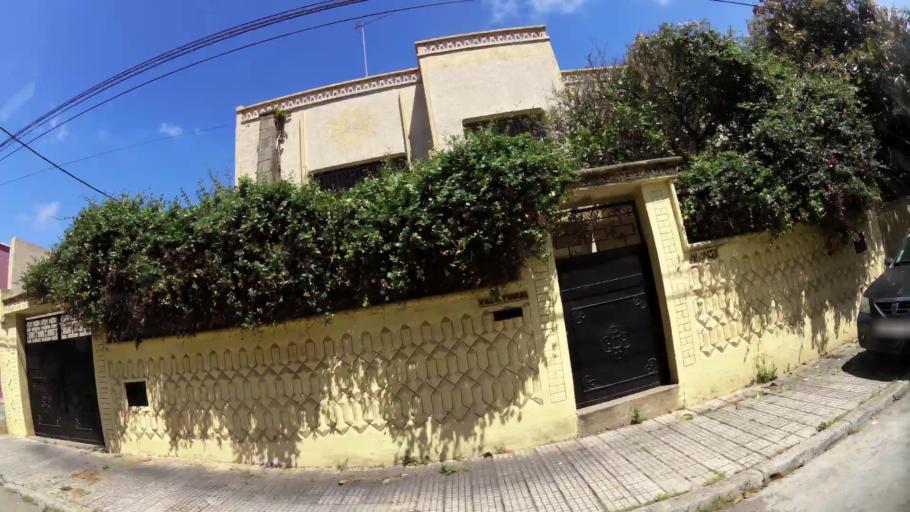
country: MA
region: Rabat-Sale-Zemmour-Zaer
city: Sale
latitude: 34.0434
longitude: -6.7864
